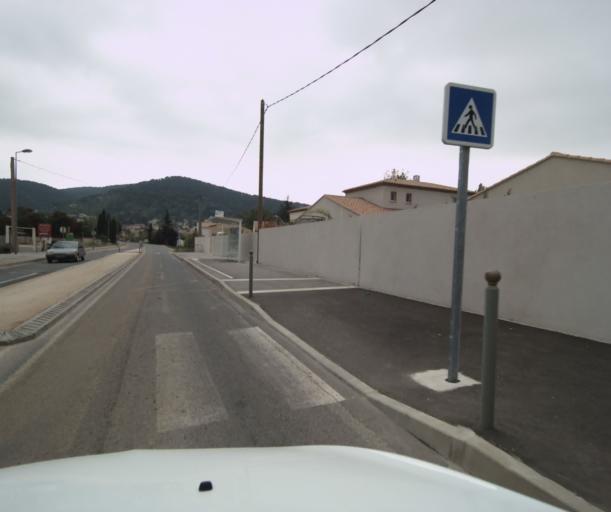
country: FR
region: Provence-Alpes-Cote d'Azur
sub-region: Departement du Var
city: La Crau
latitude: 43.1244
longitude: 6.0732
